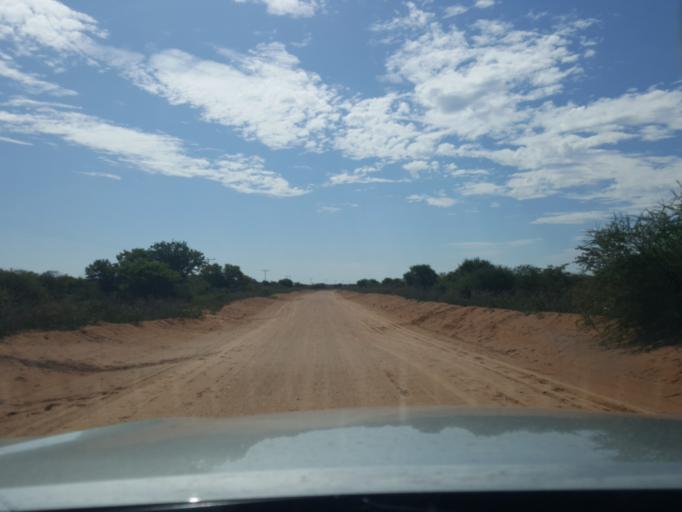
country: BW
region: Kweneng
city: Khudumelapye
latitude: -23.8617
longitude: 24.8858
